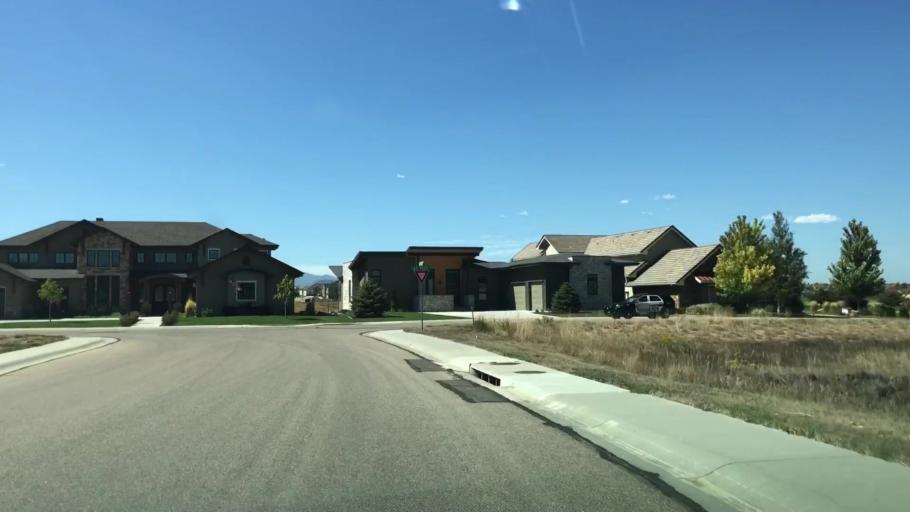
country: US
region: Colorado
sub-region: Weld County
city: Windsor
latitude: 40.4546
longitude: -104.9615
